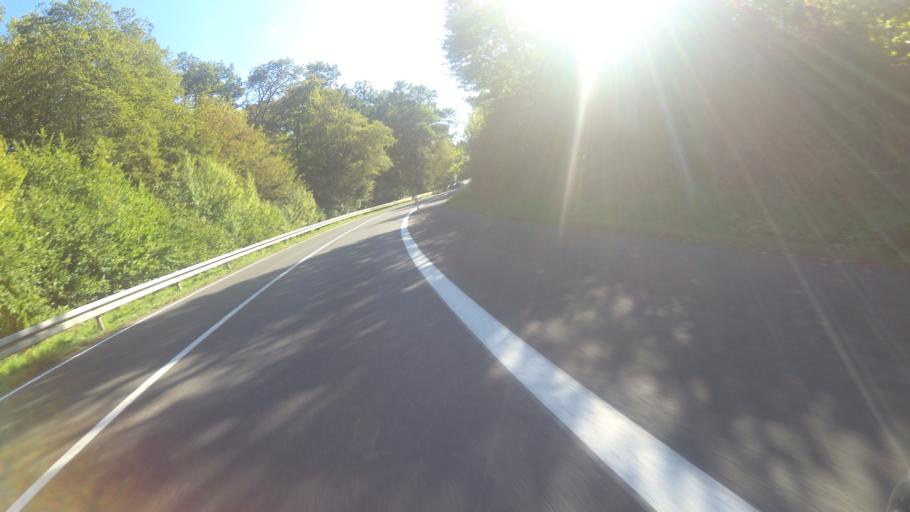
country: DE
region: Saarland
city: Eppelborn
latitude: 49.4551
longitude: 6.9630
